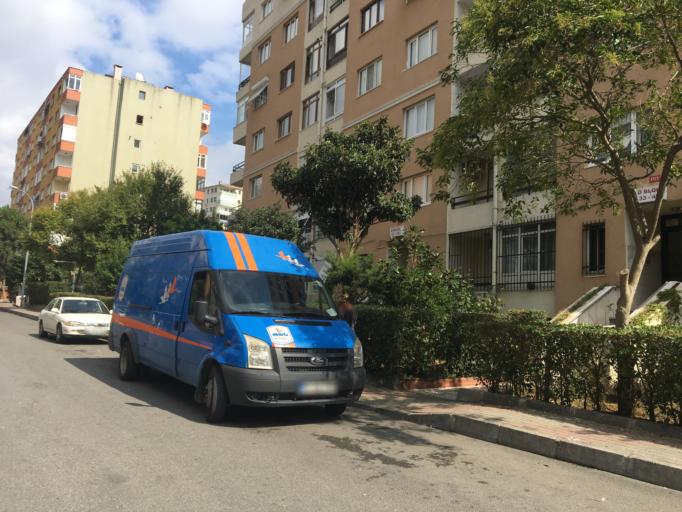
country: TR
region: Istanbul
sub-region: Atasehir
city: Atasehir
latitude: 40.9654
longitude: 29.0972
